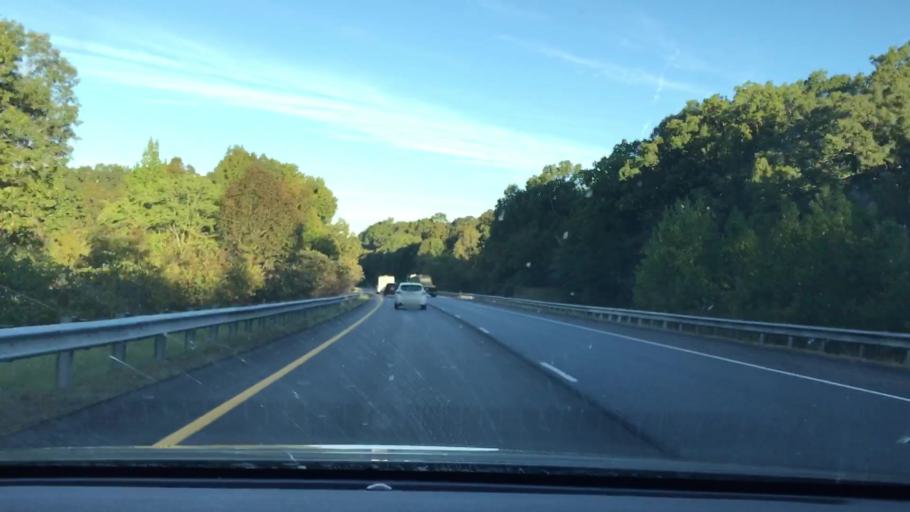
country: US
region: Tennessee
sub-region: Robertson County
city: Coopertown
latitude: 36.3627
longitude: -86.9500
